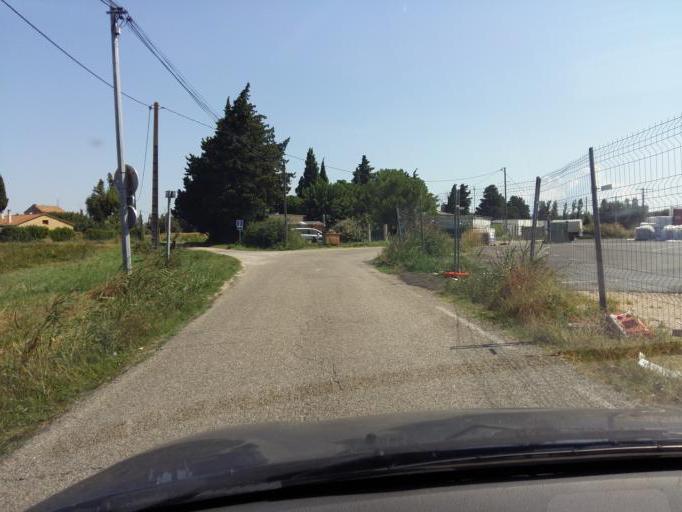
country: FR
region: Provence-Alpes-Cote d'Azur
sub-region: Departement du Vaucluse
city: Orange
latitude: 44.1229
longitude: 4.7856
